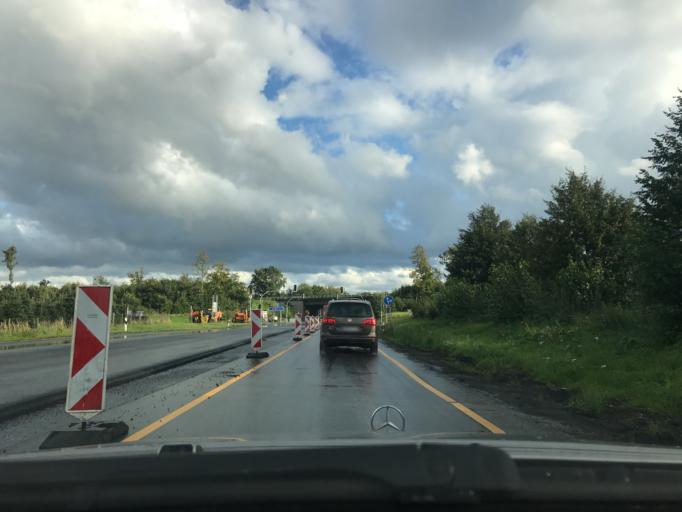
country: DE
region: North Rhine-Westphalia
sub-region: Regierungsbezirk Arnsberg
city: Bad Sassendorf
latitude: 51.5542
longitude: 8.1588
